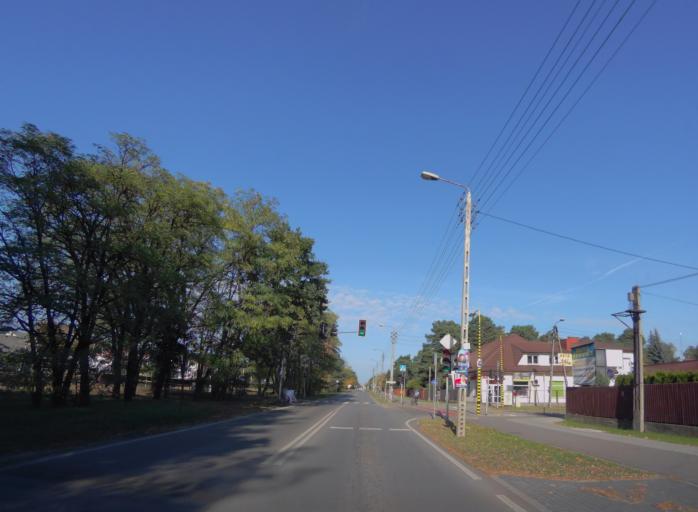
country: PL
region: Masovian Voivodeship
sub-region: Powiat otwocki
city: Jozefow
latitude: 52.1471
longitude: 21.2262
